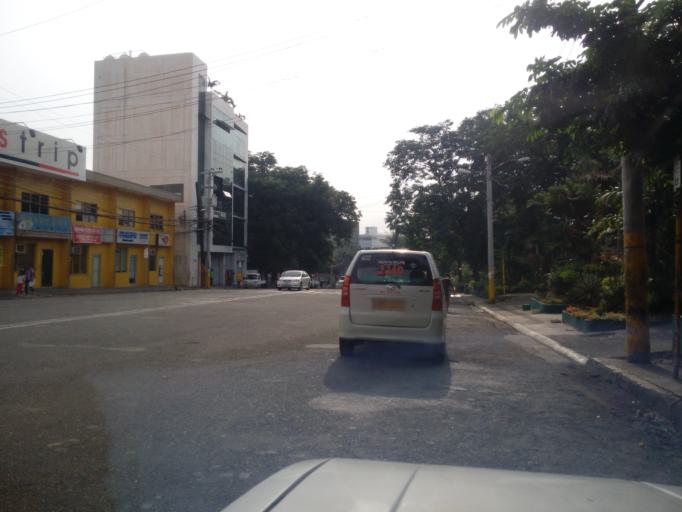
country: PH
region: Central Visayas
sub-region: Province of Cebu
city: Cebu City
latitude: 10.3049
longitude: 123.8990
